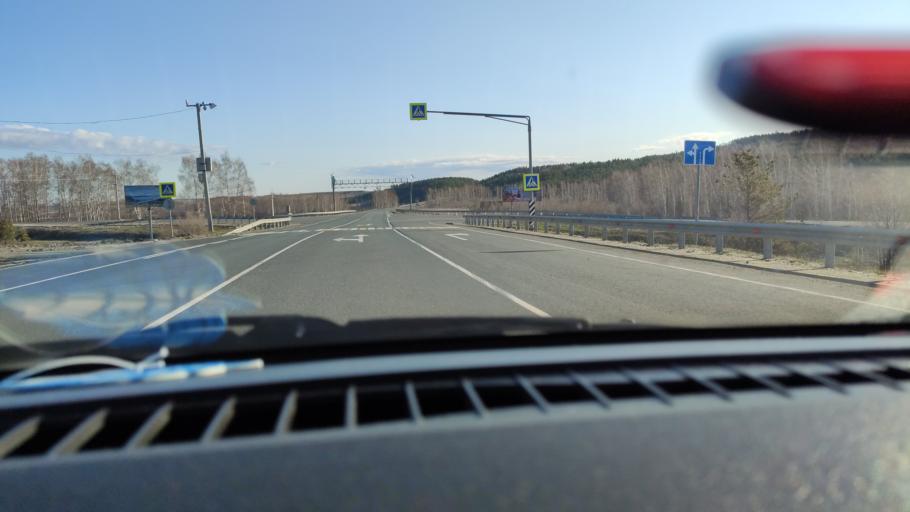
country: RU
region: Saratov
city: Khvalynsk
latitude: 52.5247
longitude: 48.0224
